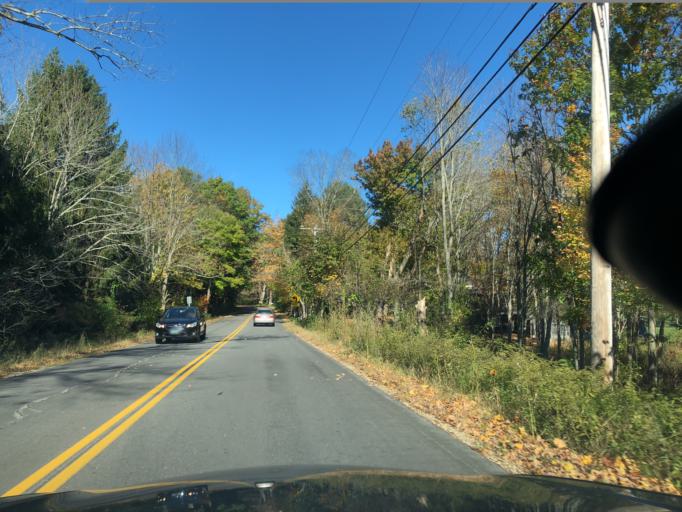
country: US
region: New Hampshire
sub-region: Rockingham County
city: Newmarket
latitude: 43.1103
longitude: -70.9595
